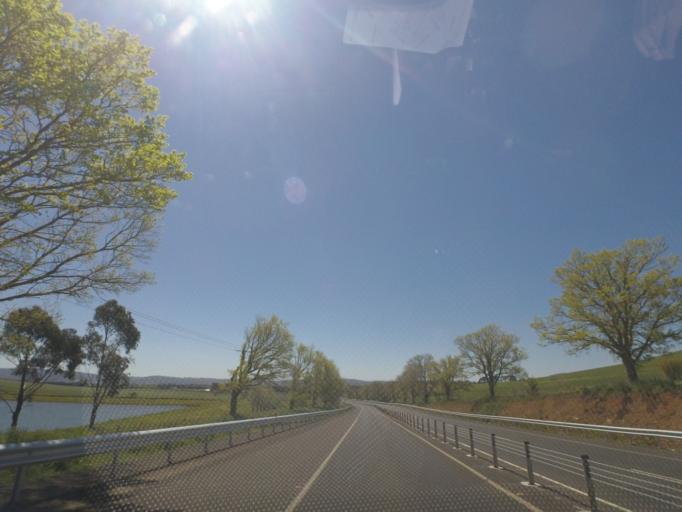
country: AU
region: Victoria
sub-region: Hume
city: Sunbury
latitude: -37.3008
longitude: 144.7367
